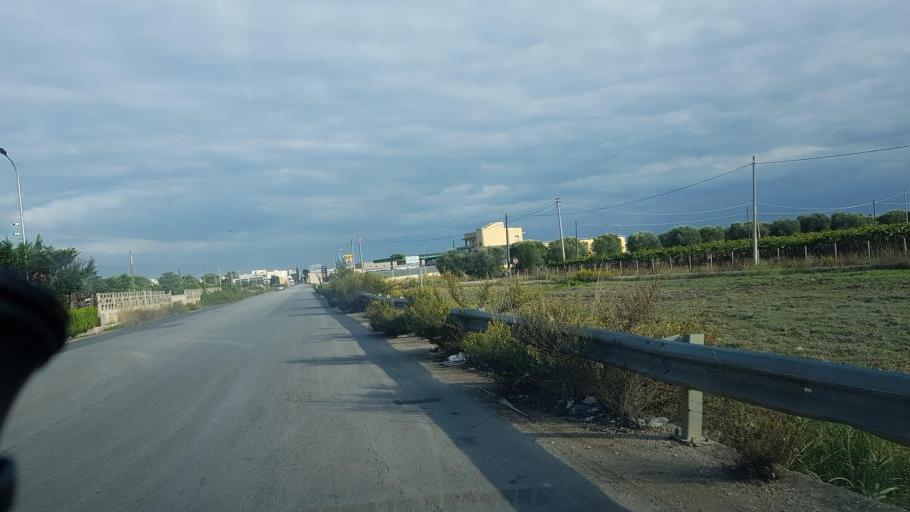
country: IT
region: Apulia
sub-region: Provincia di Brindisi
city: Francavilla Fontana
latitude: 40.5309
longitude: 17.5668
